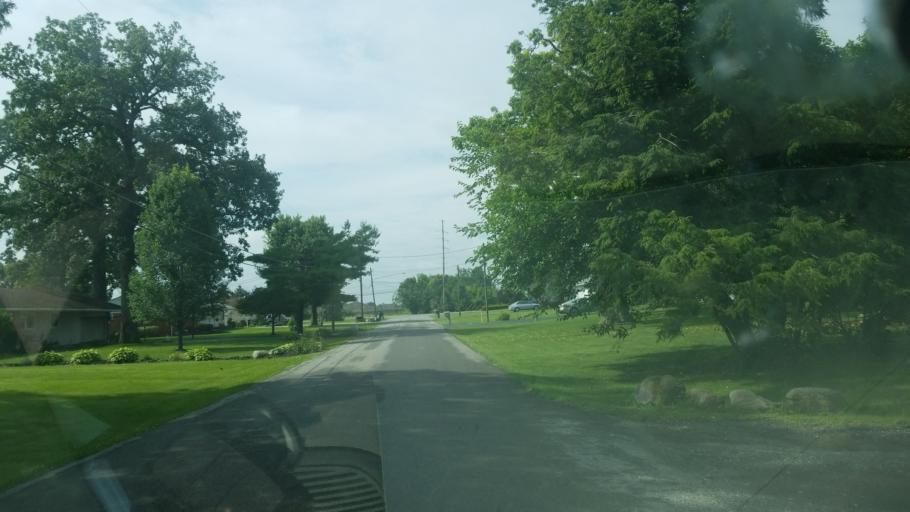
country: US
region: Ohio
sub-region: Marion County
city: Marion
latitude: 40.5654
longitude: -83.1090
